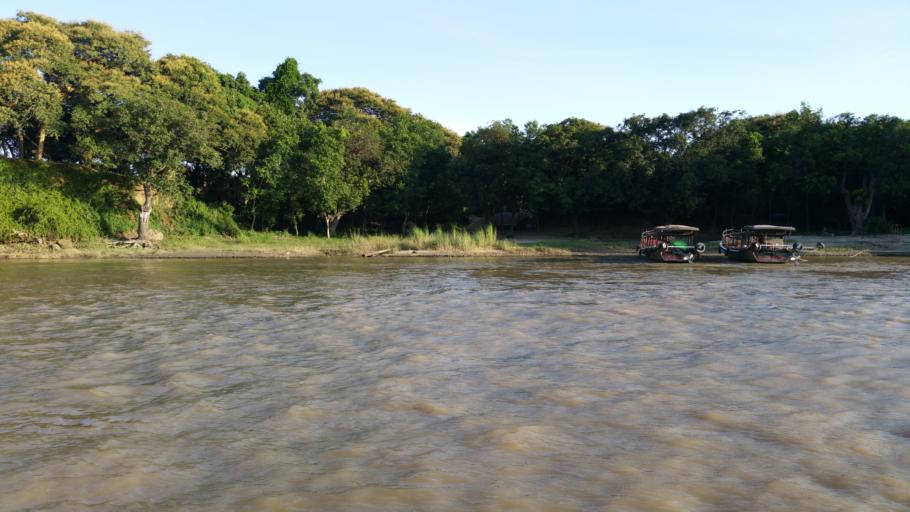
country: MM
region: Magway
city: Pakokku
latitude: 21.1844
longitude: 94.8679
